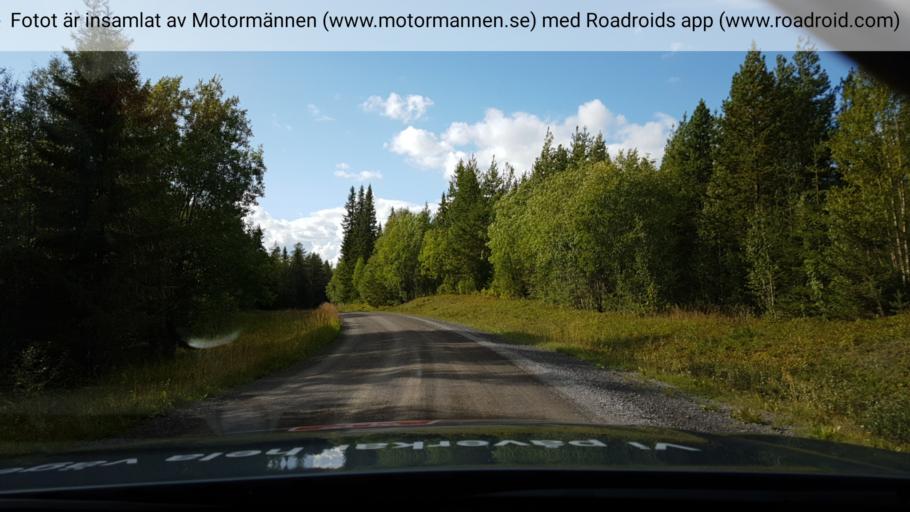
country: SE
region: Jaemtland
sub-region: OEstersunds Kommun
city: Lit
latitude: 63.3221
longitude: 15.2187
